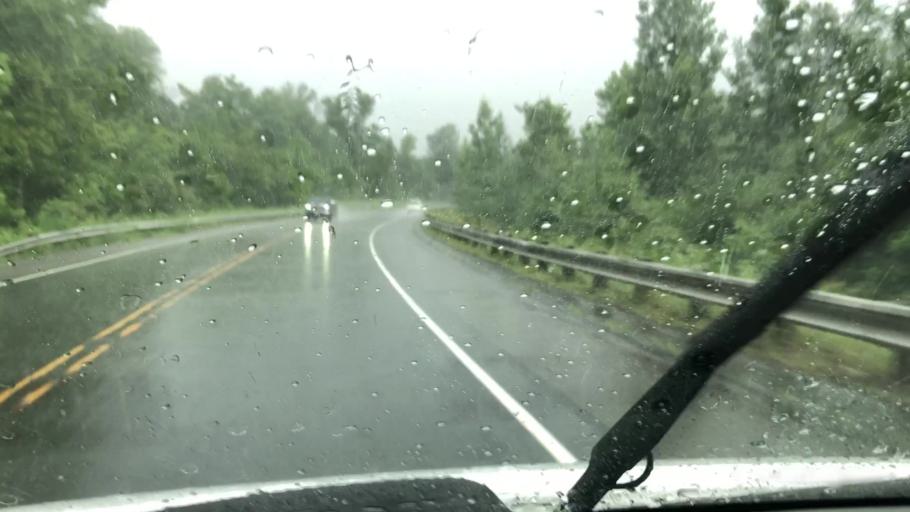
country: US
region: Massachusetts
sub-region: Berkshire County
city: Pittsfield
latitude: 42.4147
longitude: -73.2741
